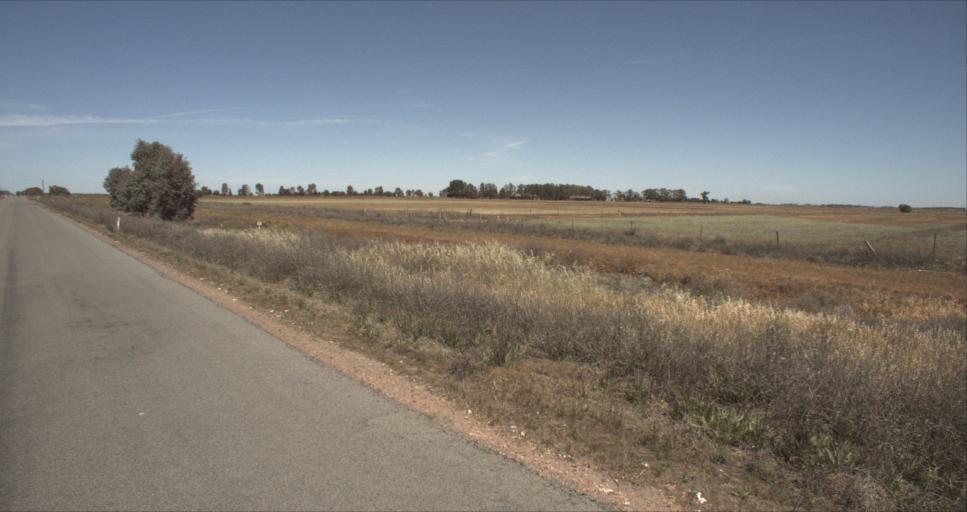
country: AU
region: New South Wales
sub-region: Leeton
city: Leeton
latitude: -34.4364
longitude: 146.2986
